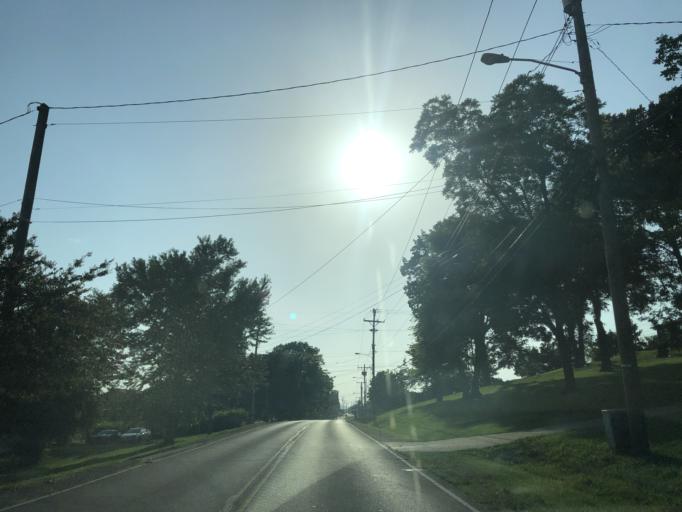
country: US
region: Tennessee
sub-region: Davidson County
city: Lakewood
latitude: 36.1503
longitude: -86.6626
